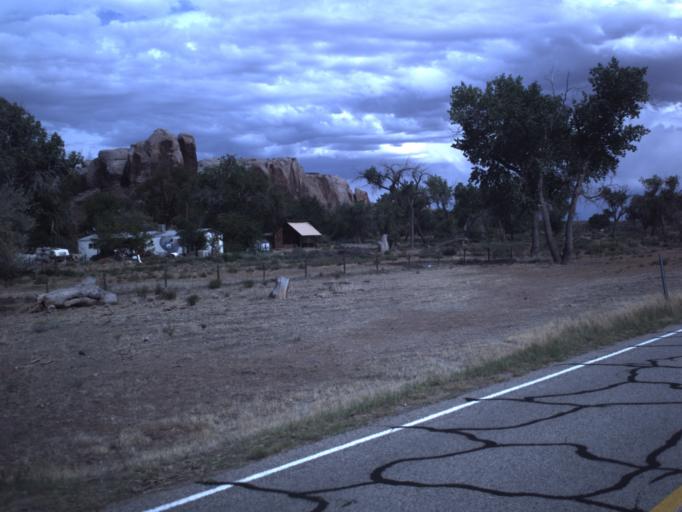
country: US
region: Utah
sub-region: San Juan County
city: Blanding
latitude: 37.2842
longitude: -109.5168
